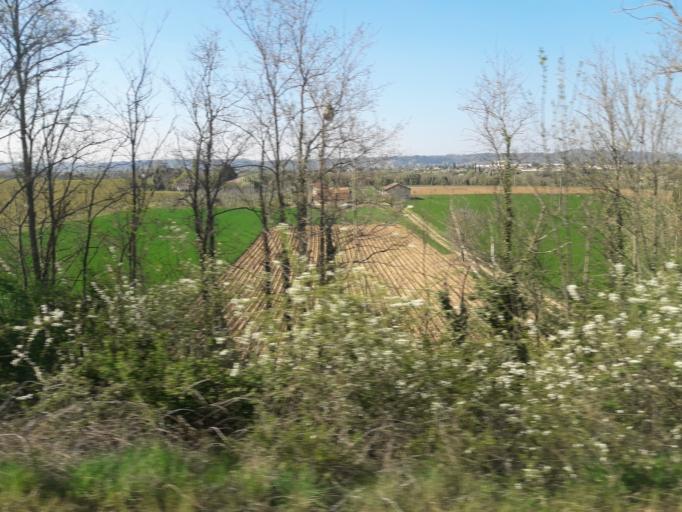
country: FR
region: Rhone-Alpes
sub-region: Departement de la Drome
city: Romans-sur-Isere
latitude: 45.0250
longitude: 5.0226
